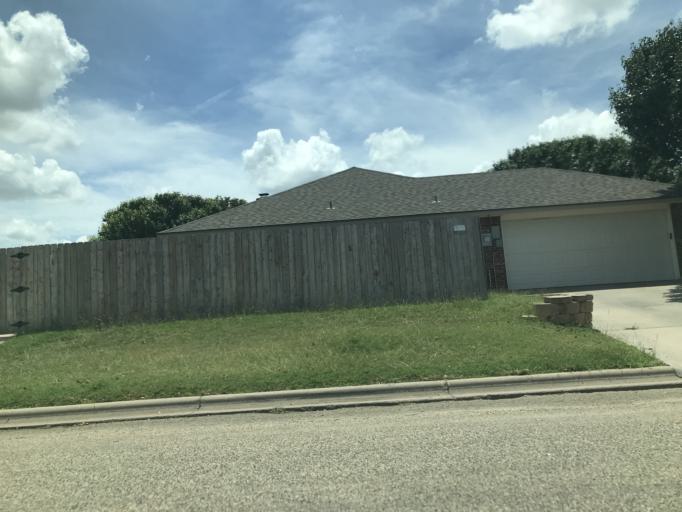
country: US
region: Texas
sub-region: Taylor County
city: Abilene
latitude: 32.4861
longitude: -99.6860
